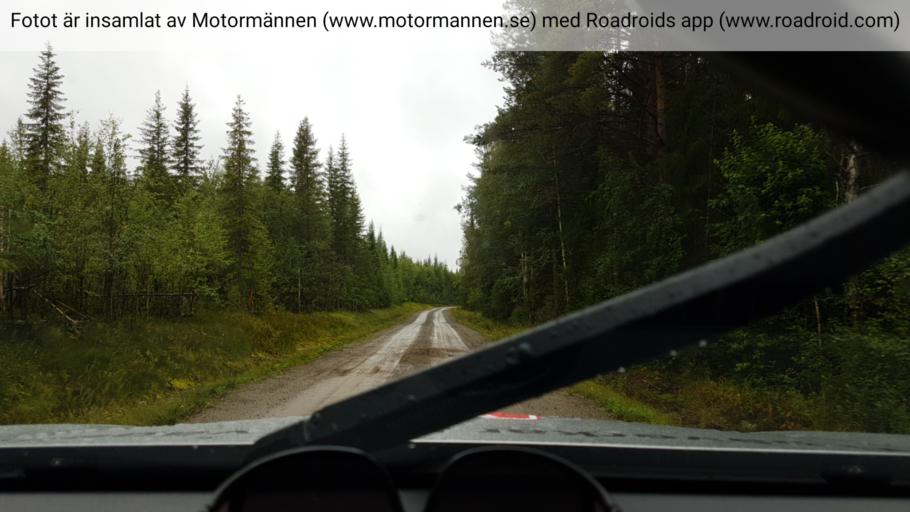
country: SE
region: Vaesterbotten
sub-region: Storumans Kommun
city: Storuman
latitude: 64.9090
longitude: 17.4670
